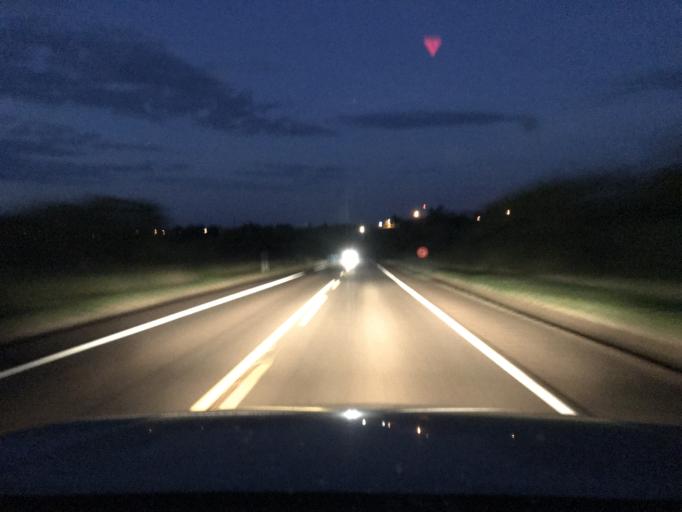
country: PY
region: Canindeyu
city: Salto del Guaira
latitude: -24.1053
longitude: -54.2367
